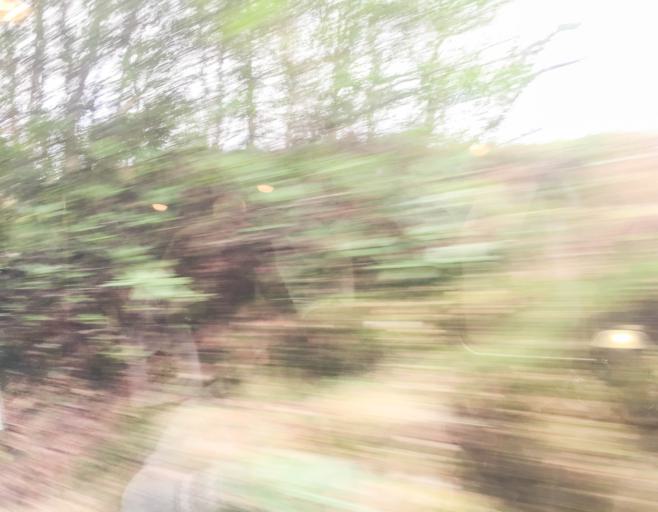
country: GB
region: Scotland
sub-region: Argyll and Bute
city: Garelochhead
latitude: 56.2180
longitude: -4.6996
